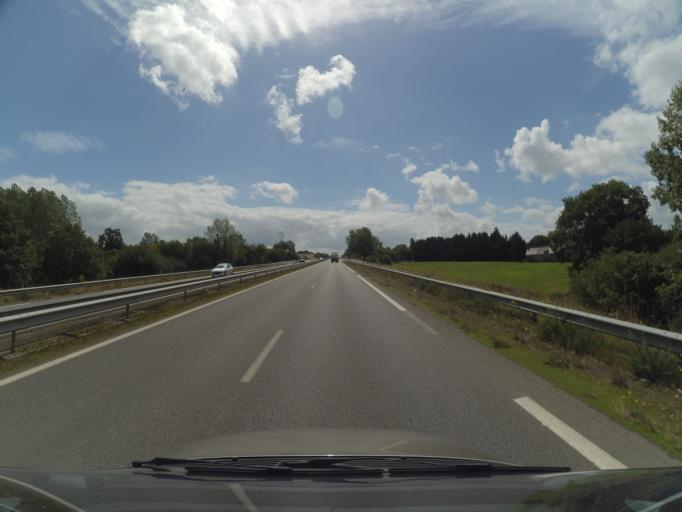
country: FR
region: Brittany
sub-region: Departement des Cotes-d'Armor
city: Saint-Brieuc
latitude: 48.4880
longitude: -2.7641
